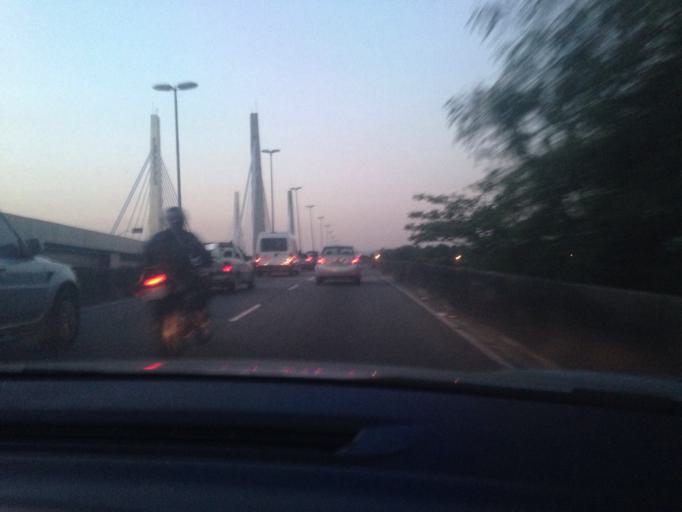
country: BR
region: Rio de Janeiro
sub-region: Sao Joao De Meriti
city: Sao Joao de Meriti
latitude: -22.9780
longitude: -43.3651
